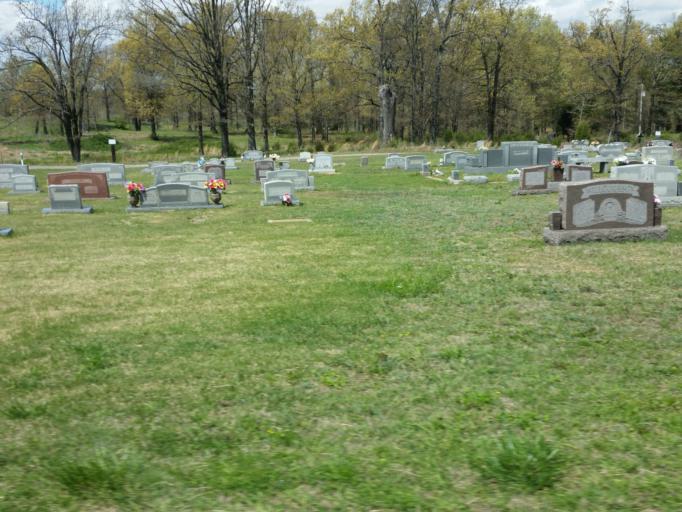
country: US
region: Arkansas
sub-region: Craighead County
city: Brookland
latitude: 36.0232
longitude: -90.6841
